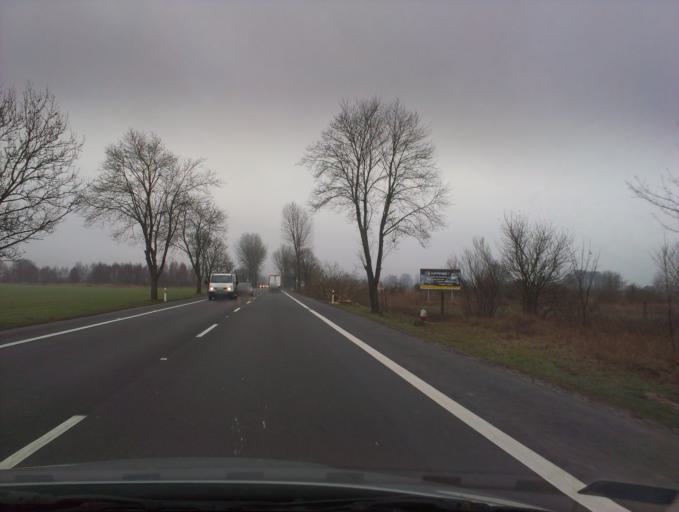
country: PL
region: Greater Poland Voivodeship
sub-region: Powiat pilski
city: Ujscie
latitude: 53.0797
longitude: 16.7318
